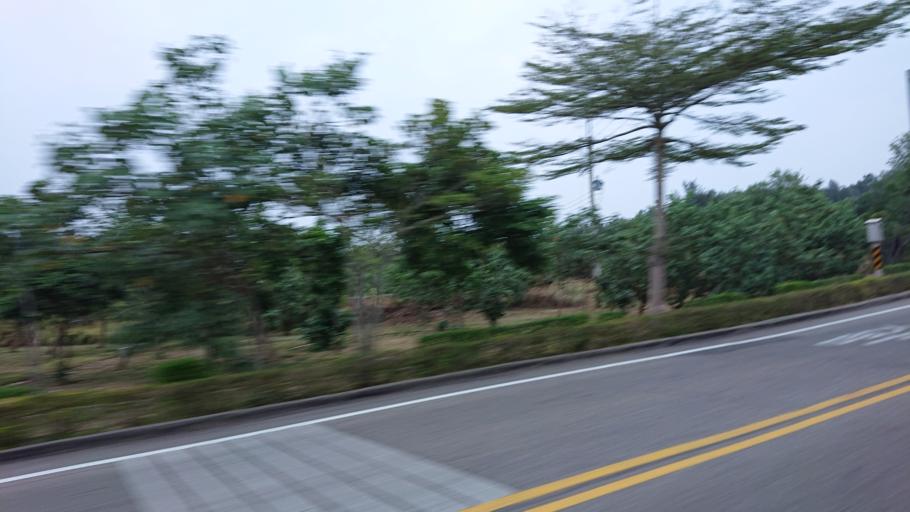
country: TW
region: Fukien
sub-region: Kinmen
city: Jincheng
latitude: 24.4267
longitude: 118.2529
